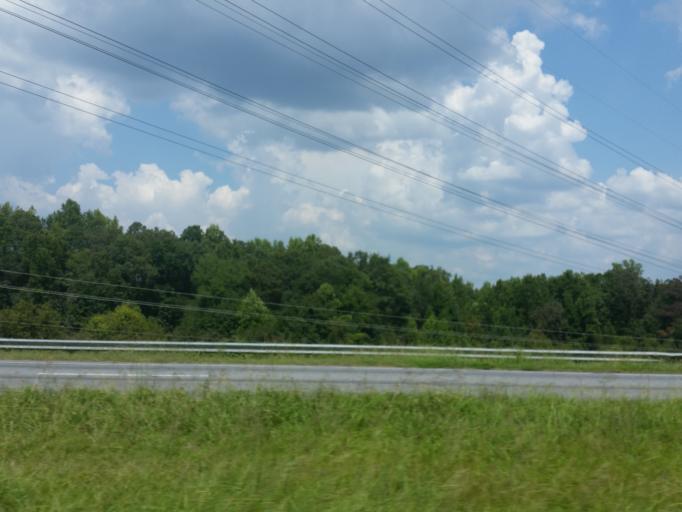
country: US
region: North Carolina
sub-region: Cleveland County
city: White Plains
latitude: 35.2477
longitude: -81.4441
